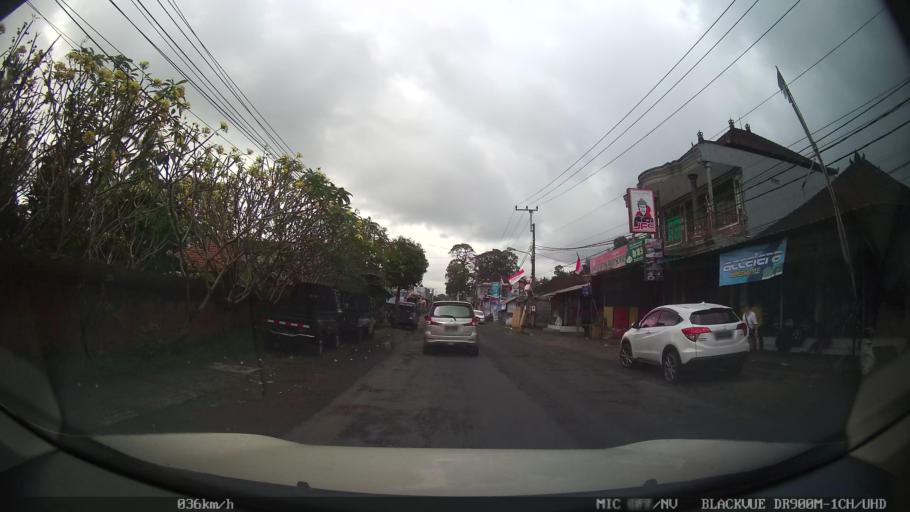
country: ID
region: Bali
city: Banjar Keraman
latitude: -8.5253
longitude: 115.2113
